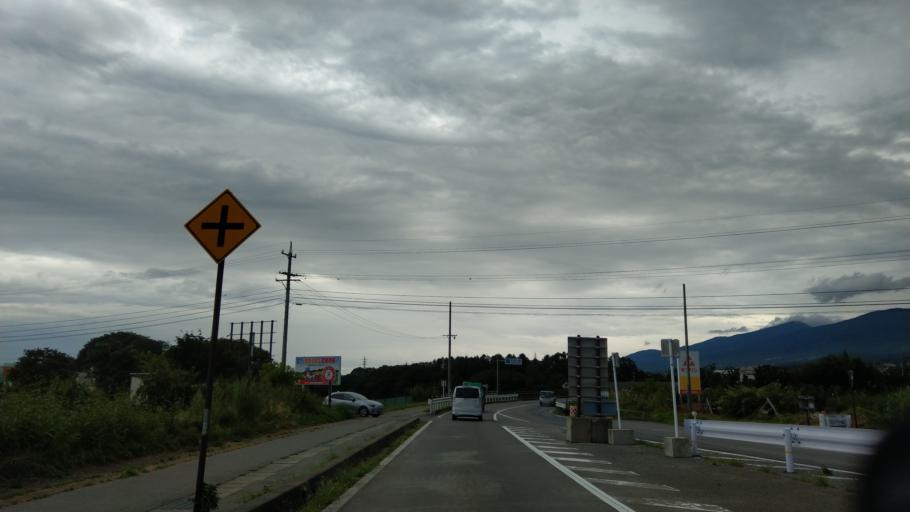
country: JP
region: Nagano
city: Komoro
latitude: 36.3067
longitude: 138.4578
